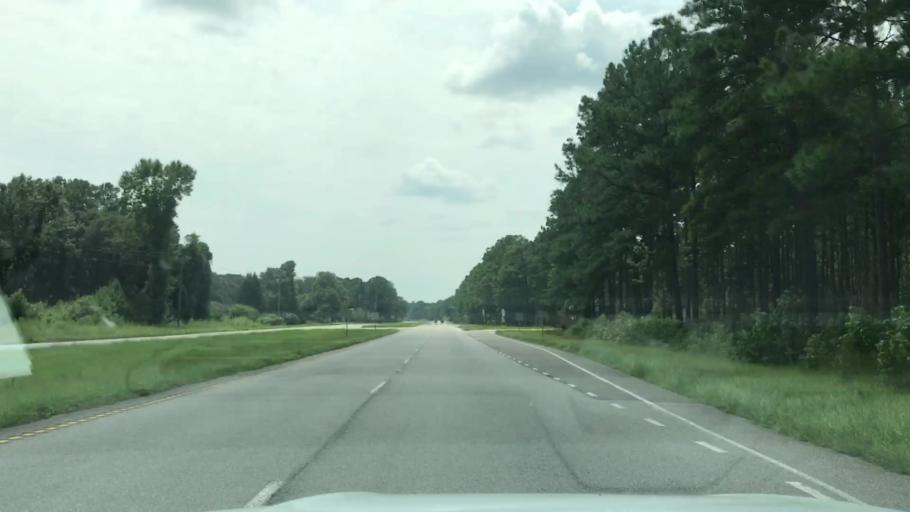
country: US
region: South Carolina
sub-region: Charleston County
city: Awendaw
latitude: 33.0361
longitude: -79.6187
